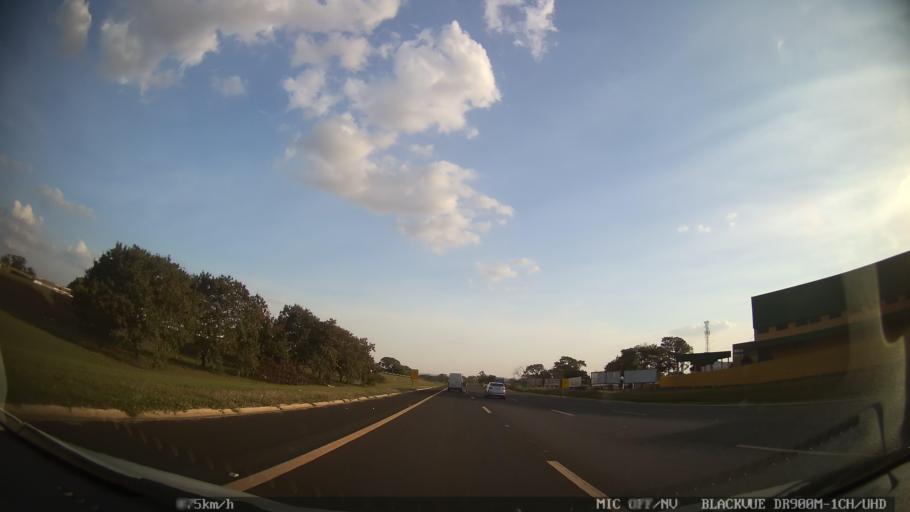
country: BR
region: Sao Paulo
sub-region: Ribeirao Preto
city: Ribeirao Preto
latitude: -21.1145
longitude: -47.7822
